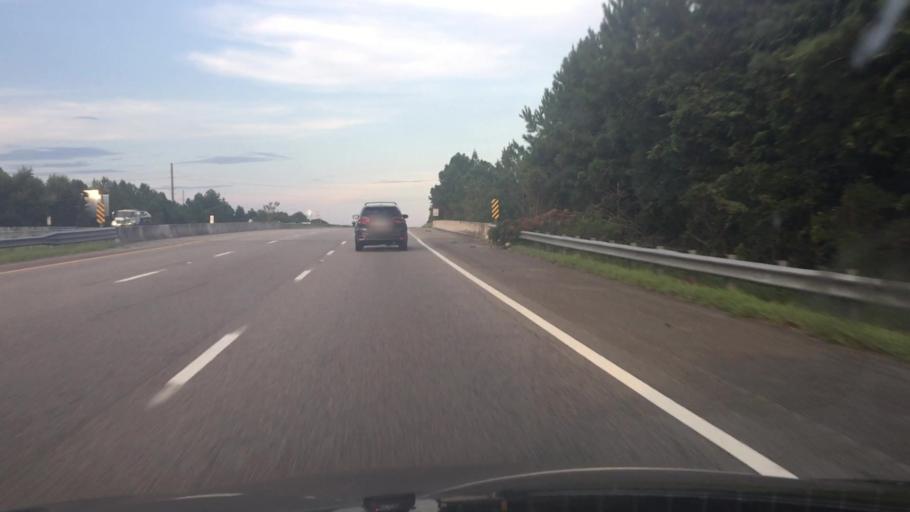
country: US
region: South Carolina
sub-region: Horry County
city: Forestbrook
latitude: 33.7419
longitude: -78.9396
